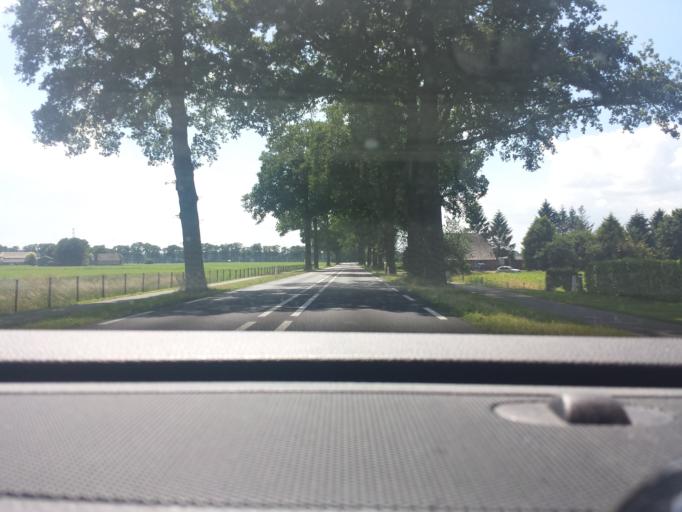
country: NL
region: Gelderland
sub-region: Gemeente Lochem
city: Lochem
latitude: 52.1694
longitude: 6.4549
